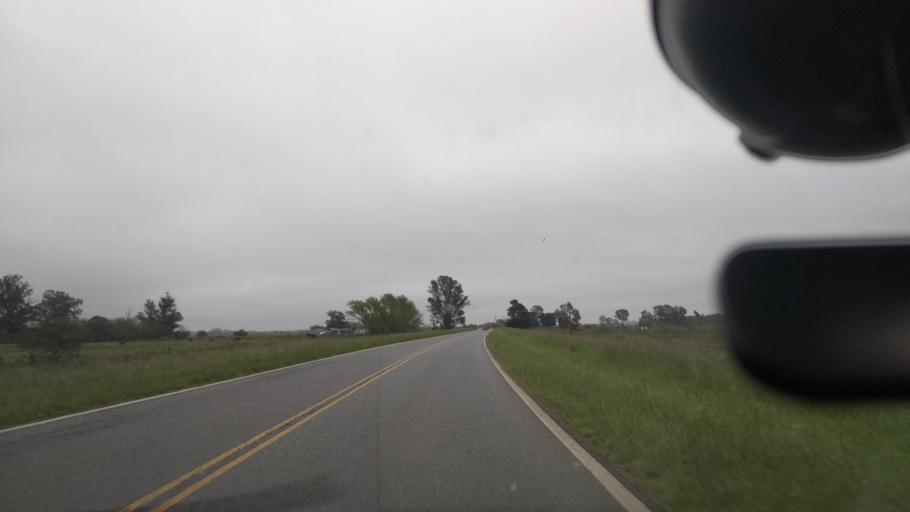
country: AR
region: Buenos Aires
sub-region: Partido de Magdalena
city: Magdalena
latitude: -35.2639
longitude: -57.6292
